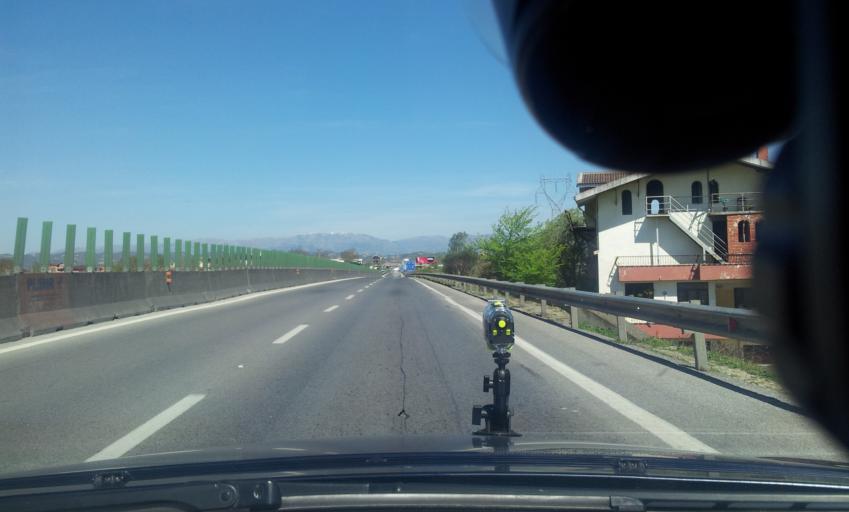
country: AL
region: Durres
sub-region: Rrethi i Durresit
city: Xhafzotaj
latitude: 41.3606
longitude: 19.5407
